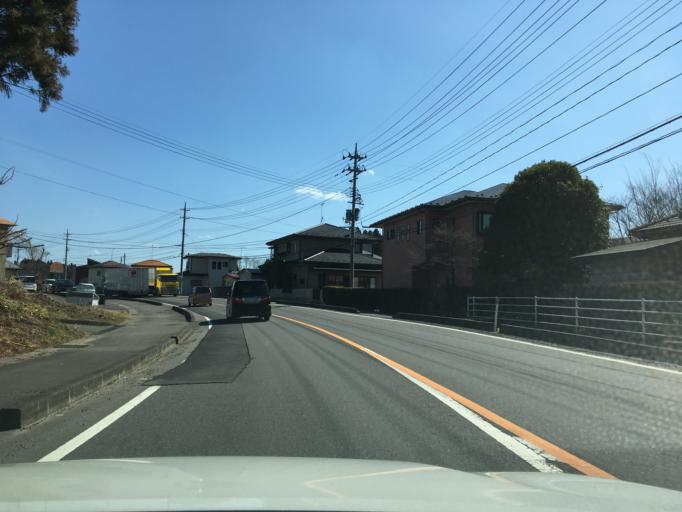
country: JP
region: Tochigi
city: Kuroiso
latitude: 37.1072
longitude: 140.1632
